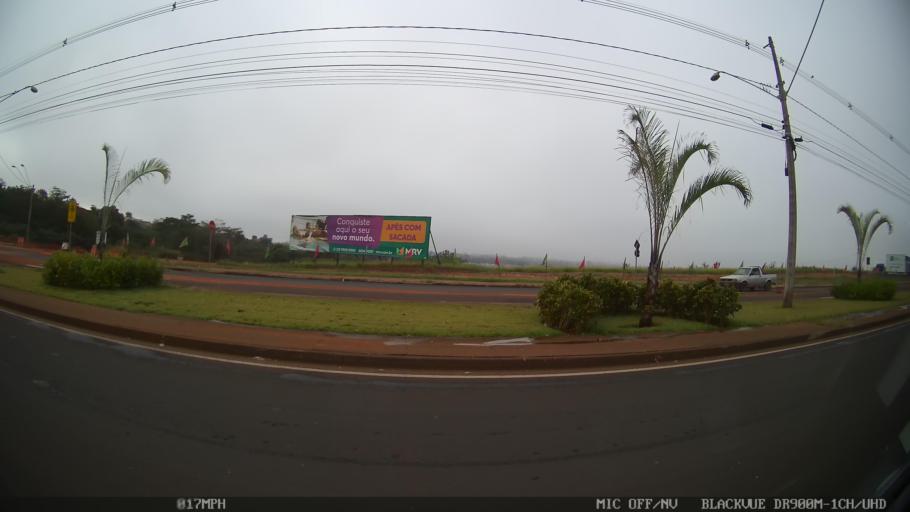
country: BR
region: Sao Paulo
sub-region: Sao Jose Do Rio Preto
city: Sao Jose do Rio Preto
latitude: -20.8505
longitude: -49.3703
